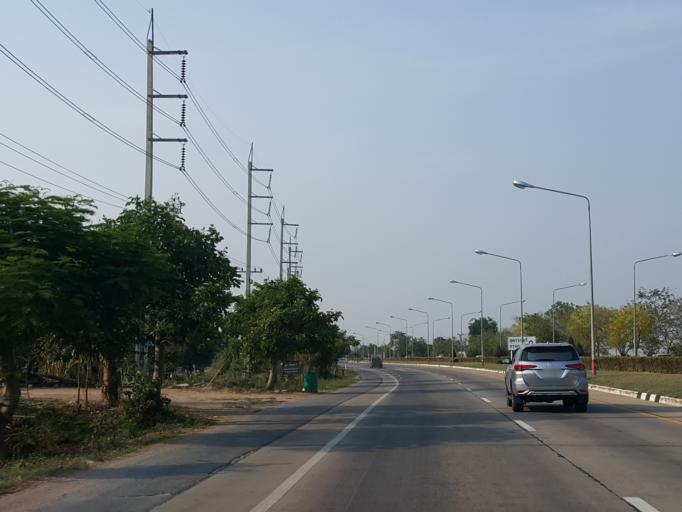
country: TH
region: Suphan Buri
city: Doem Bang Nang Buat
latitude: 14.9188
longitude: 100.0845
